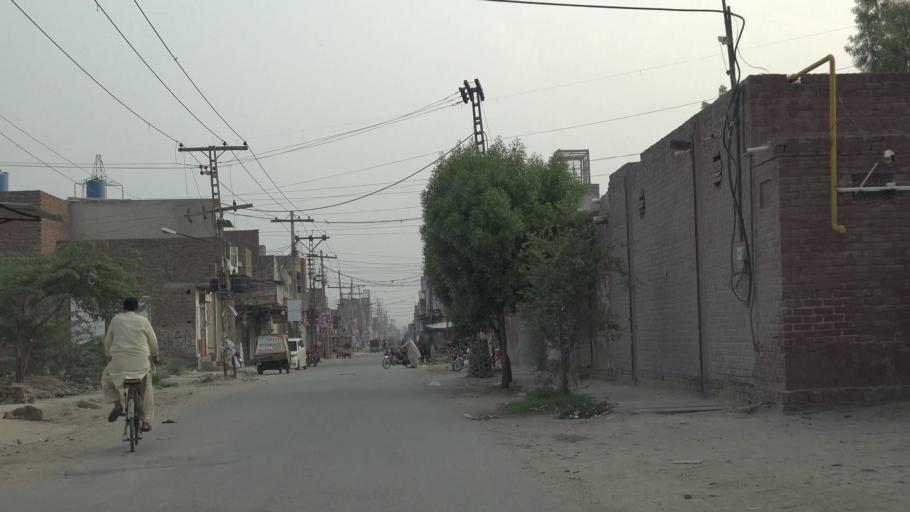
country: PK
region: Punjab
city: Faisalabad
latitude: 31.4316
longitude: 73.1420
